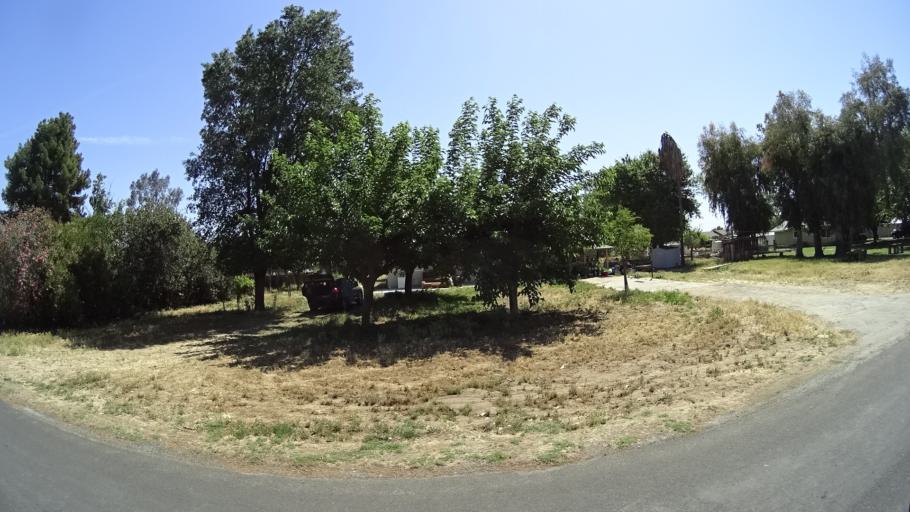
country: US
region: California
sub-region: Kings County
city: Lemoore
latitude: 36.2751
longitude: -119.7826
